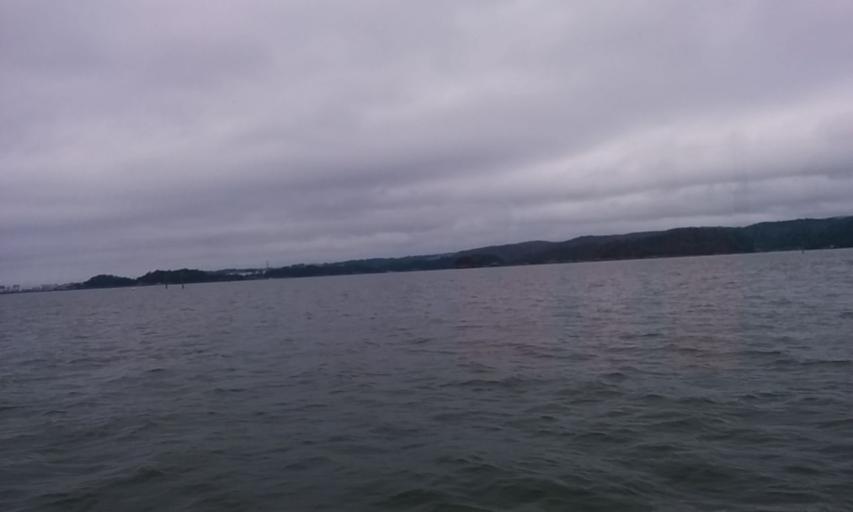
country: JP
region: Miyagi
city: Matsushima
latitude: 38.3466
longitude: 141.0760
